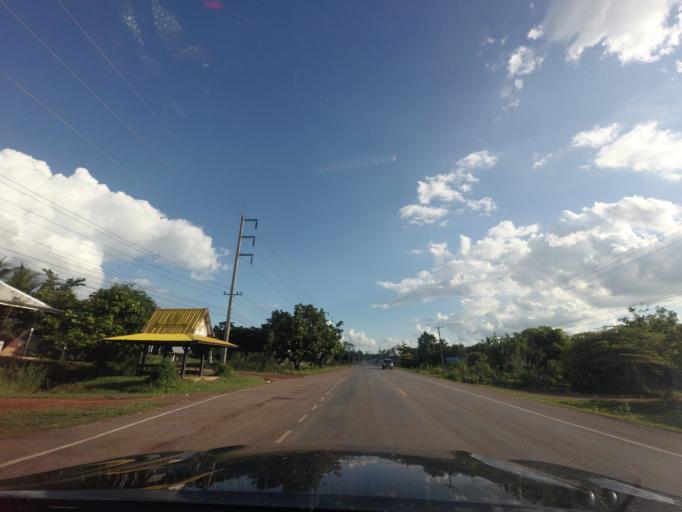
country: TH
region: Changwat Udon Thani
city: Thung Fon
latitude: 17.5030
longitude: 103.2035
